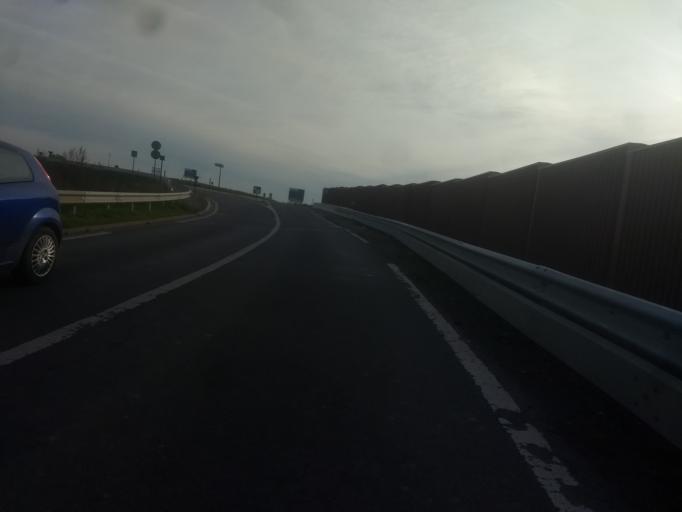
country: FR
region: Nord-Pas-de-Calais
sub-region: Departement du Pas-de-Calais
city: Agny
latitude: 50.2557
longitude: 2.7632
